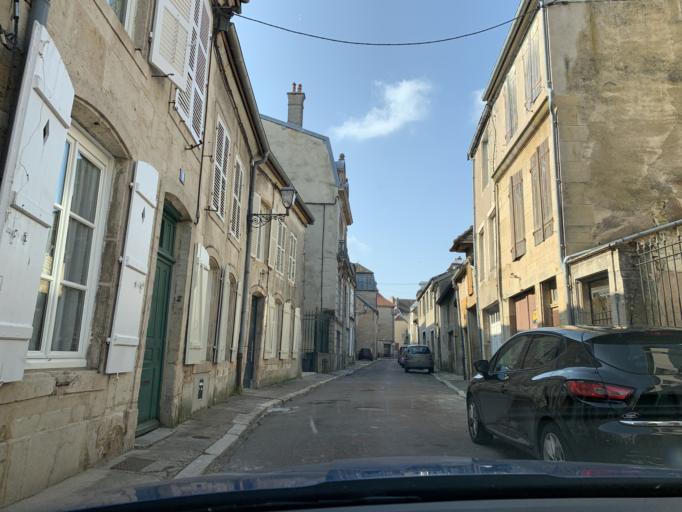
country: FR
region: Champagne-Ardenne
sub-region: Departement de la Haute-Marne
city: Langres
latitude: 47.8613
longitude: 5.3349
